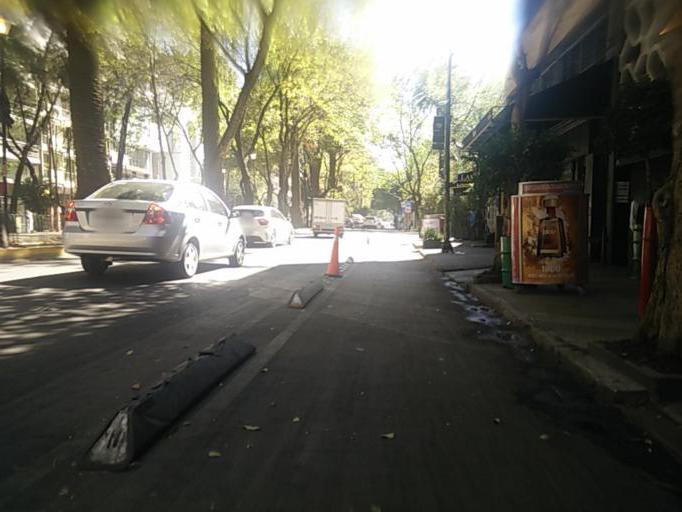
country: MX
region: Mexico City
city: Benito Juarez
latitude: 19.4096
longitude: -99.1727
